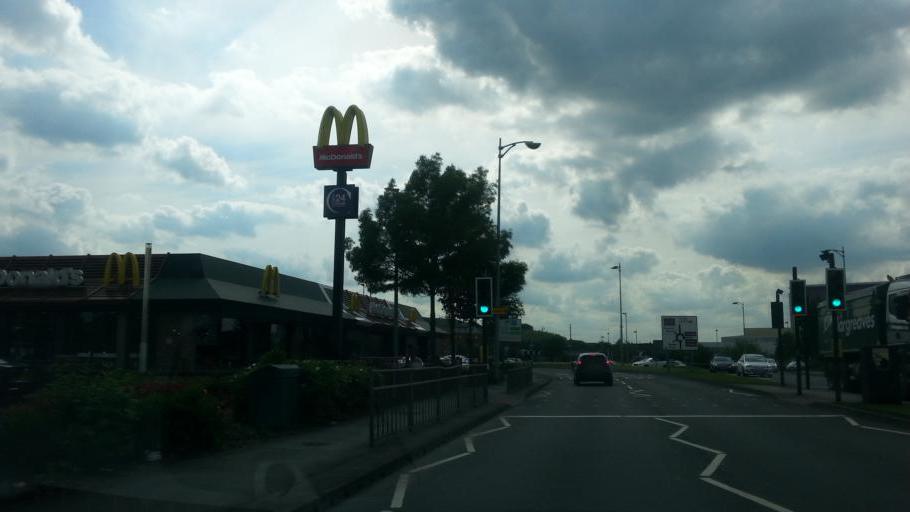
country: GB
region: England
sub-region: City and Borough of Wakefield
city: Pontefract
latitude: 53.7096
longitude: -1.3352
